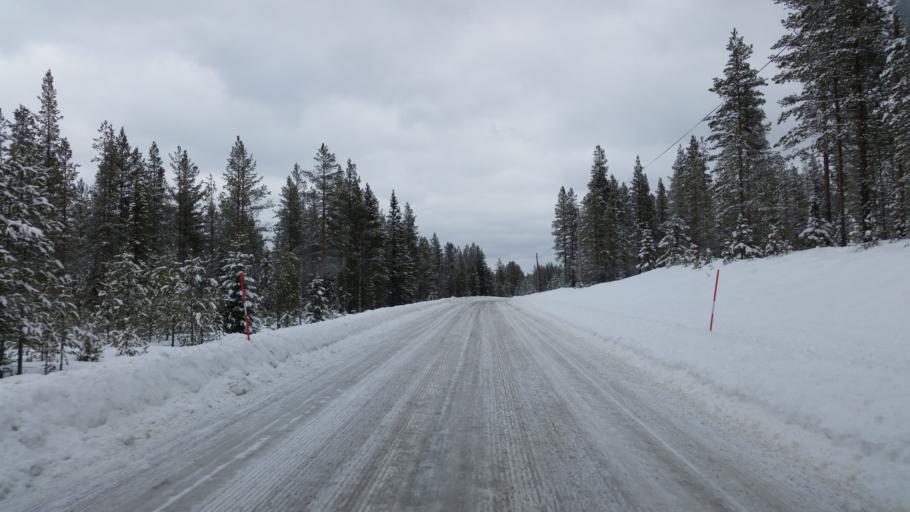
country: SE
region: Jaemtland
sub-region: Bergs Kommun
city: Hoverberg
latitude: 62.4725
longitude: 14.3483
